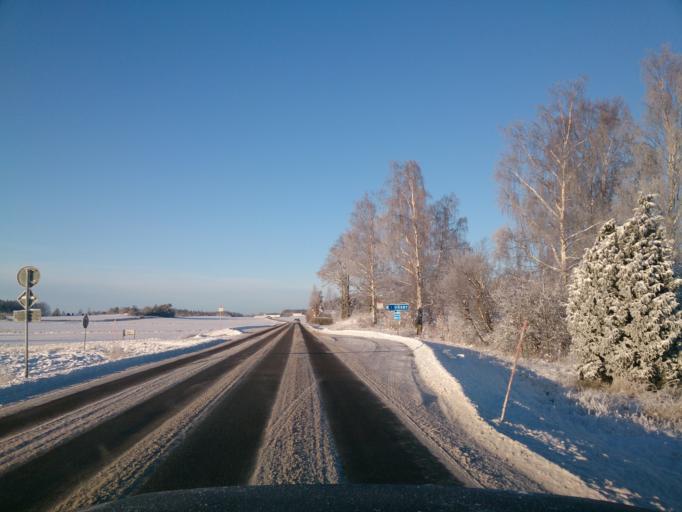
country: SE
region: OEstergoetland
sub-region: Norrkopings Kommun
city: Krokek
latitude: 58.5714
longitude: 16.4199
